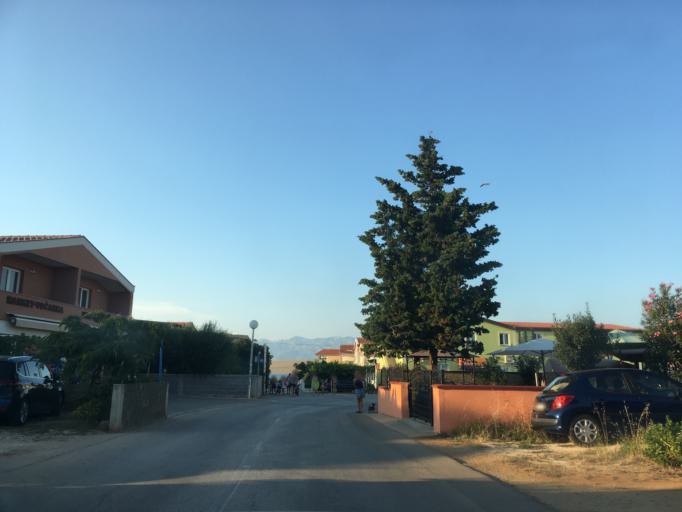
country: HR
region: Zadarska
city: Vir
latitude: 44.3048
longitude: 15.1021
